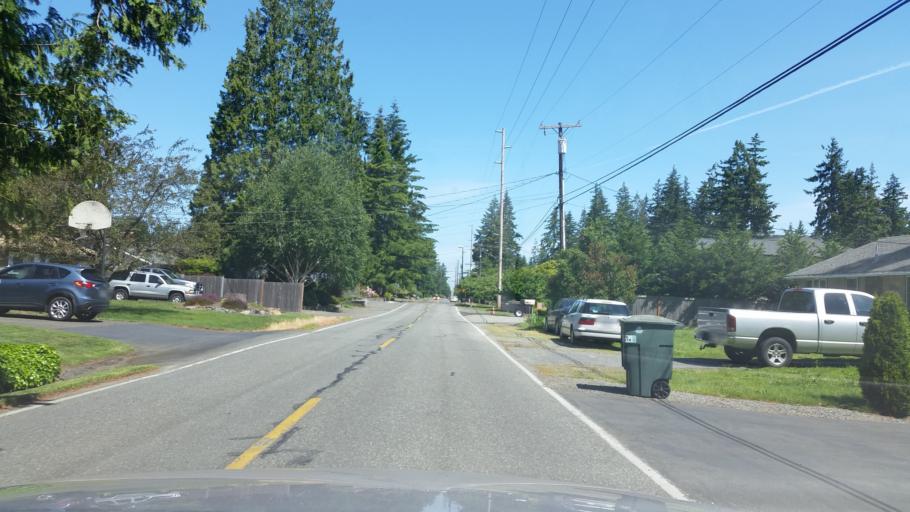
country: US
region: Washington
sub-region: Snohomish County
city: Esperance
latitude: 47.7948
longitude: -122.3616
